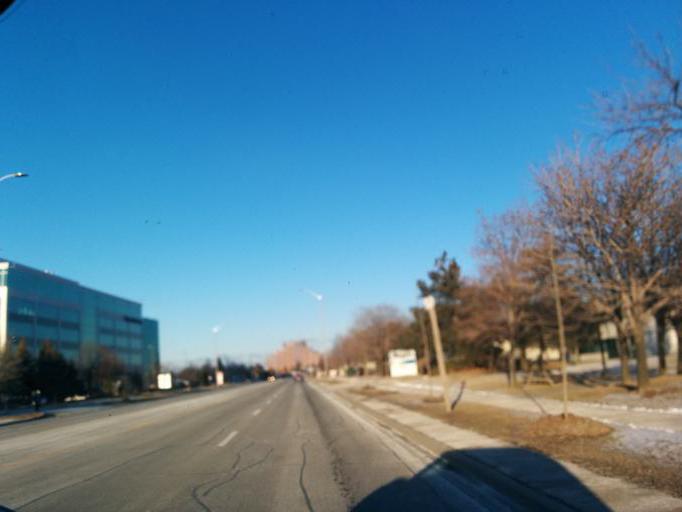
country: CA
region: Ontario
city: Etobicoke
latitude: 43.6602
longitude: -79.5997
